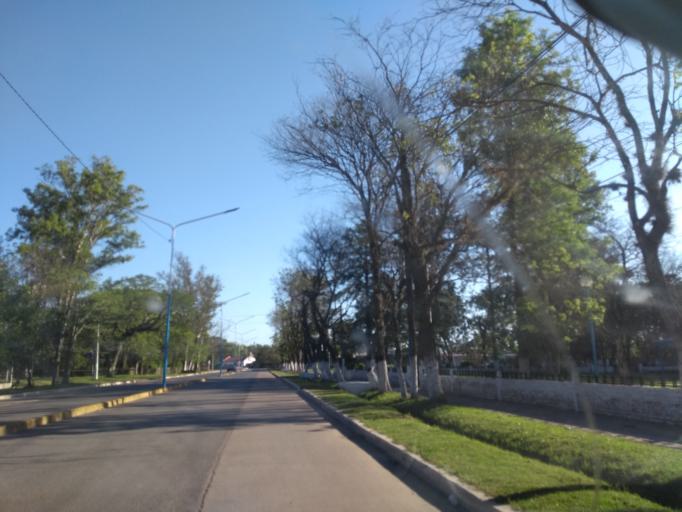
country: AR
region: Chaco
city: La Escondida
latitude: -27.1046
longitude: -59.4460
